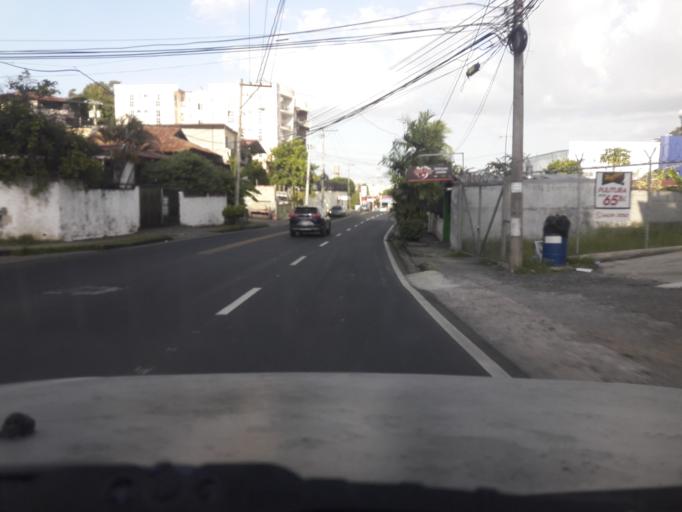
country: PA
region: Panama
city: Panama
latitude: 9.0153
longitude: -79.5061
